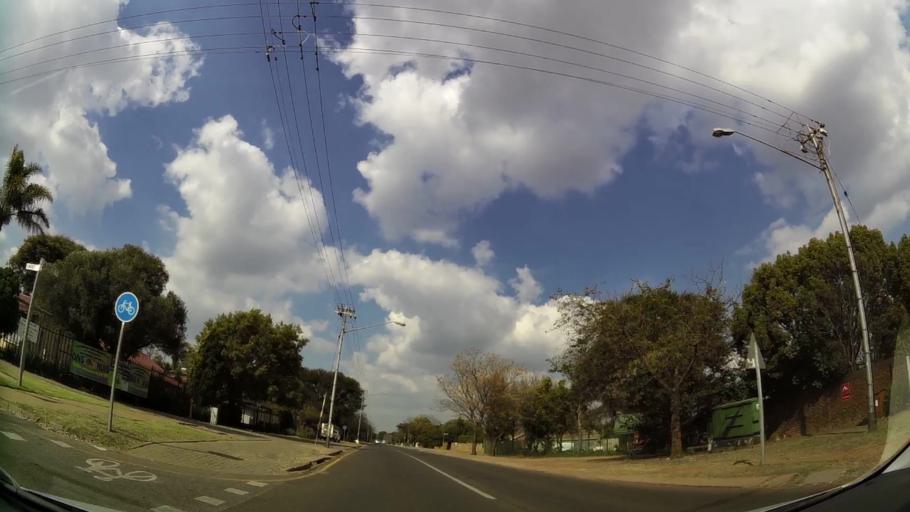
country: ZA
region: Gauteng
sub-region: City of Tshwane Metropolitan Municipality
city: Centurion
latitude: -25.8337
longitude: 28.2610
